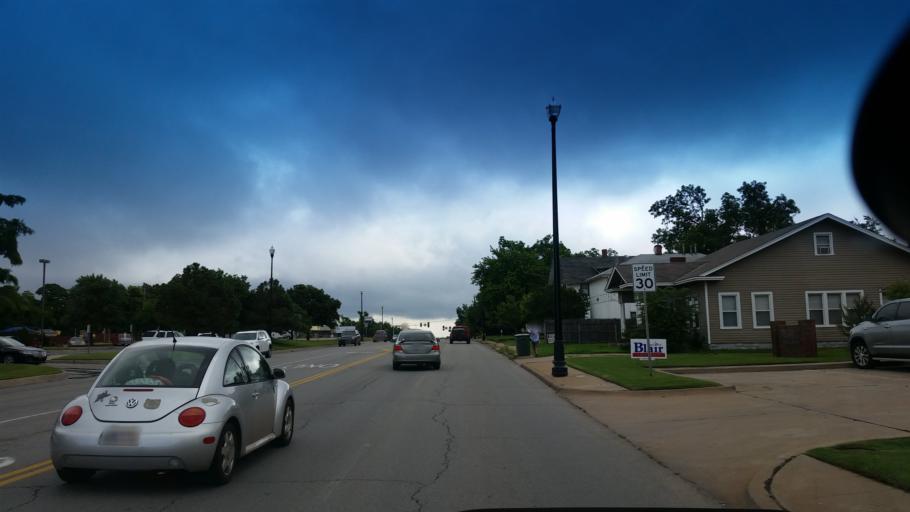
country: US
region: Oklahoma
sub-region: Oklahoma County
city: Edmond
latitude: 35.6527
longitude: -97.4778
